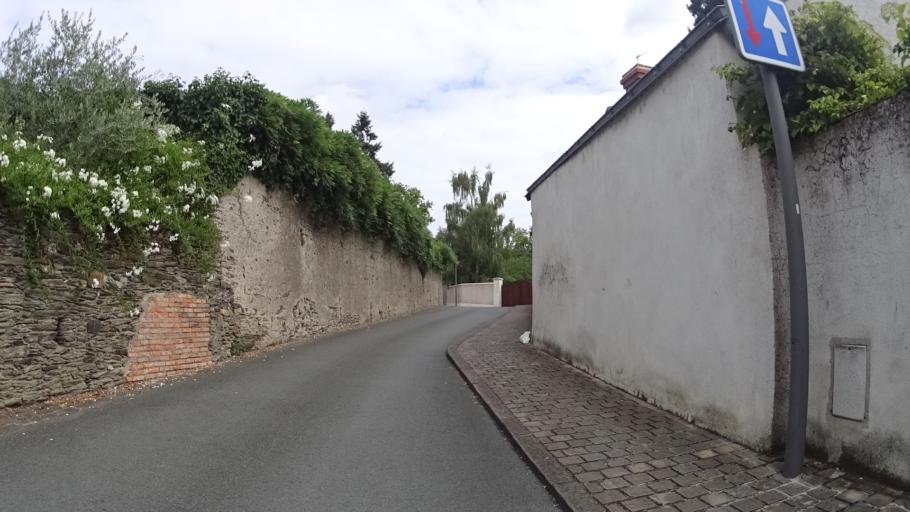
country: FR
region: Pays de la Loire
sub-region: Departement de Maine-et-Loire
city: Bouchemaine
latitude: 47.4066
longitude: -0.6209
